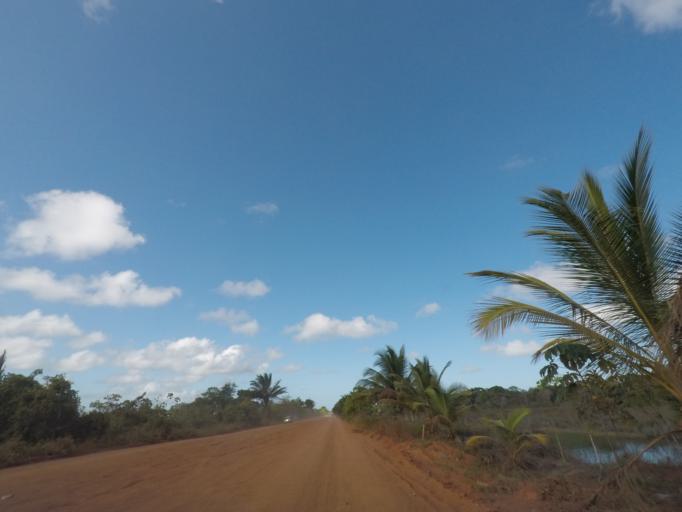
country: BR
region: Bahia
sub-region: Marau
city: Marau
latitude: -14.1615
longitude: -39.0123
